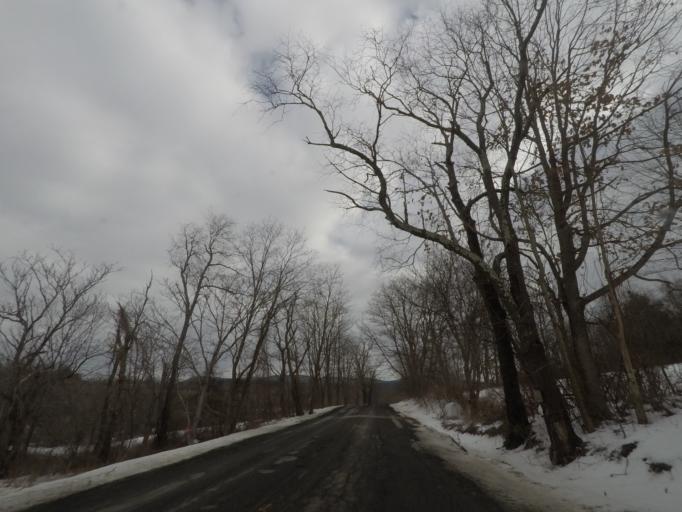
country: US
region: New York
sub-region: Rensselaer County
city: Hoosick Falls
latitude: 42.8621
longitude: -73.3584
